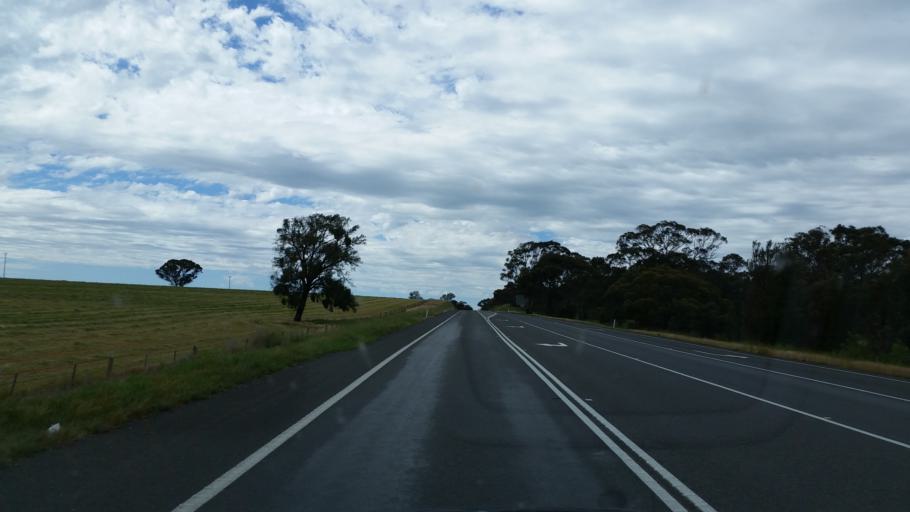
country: AU
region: South Australia
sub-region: Tatiara
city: Bordertown
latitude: -36.3468
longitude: 140.9851
